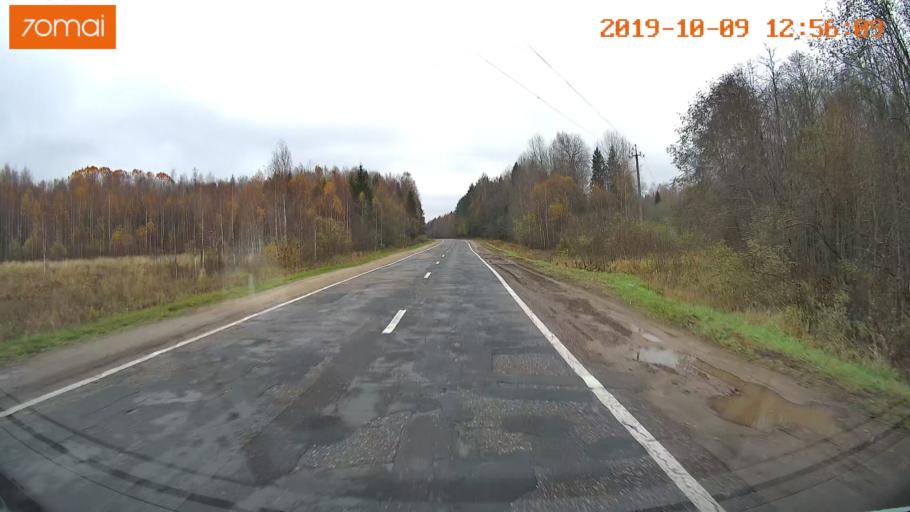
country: RU
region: Jaroslavl
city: Prechistoye
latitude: 58.3956
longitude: 40.4108
